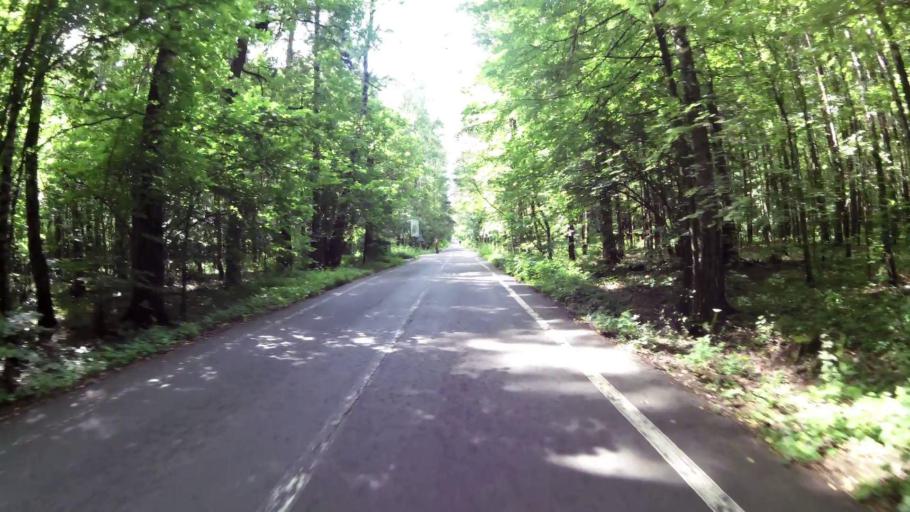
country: RU
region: Moscow
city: Babushkin
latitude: 55.8680
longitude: 37.7237
